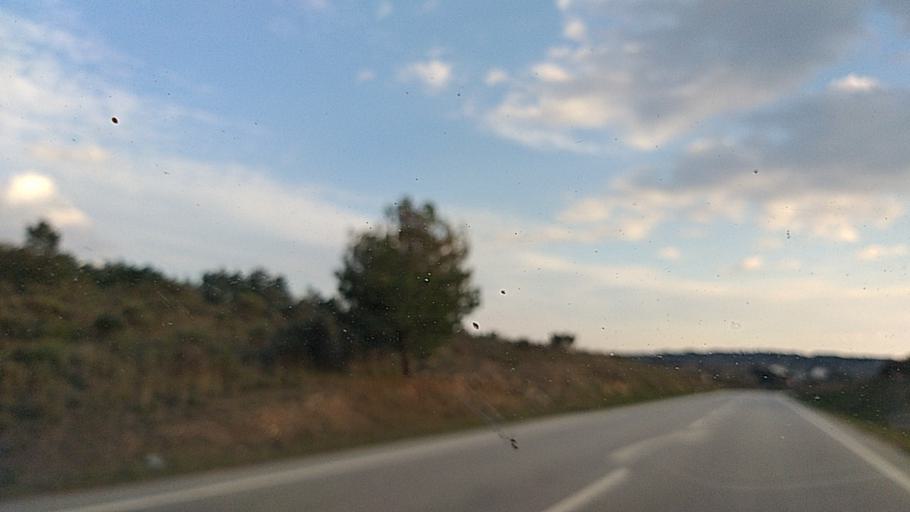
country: PT
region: Guarda
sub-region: Pinhel
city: Pinhel
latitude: 40.6781
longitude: -6.9502
